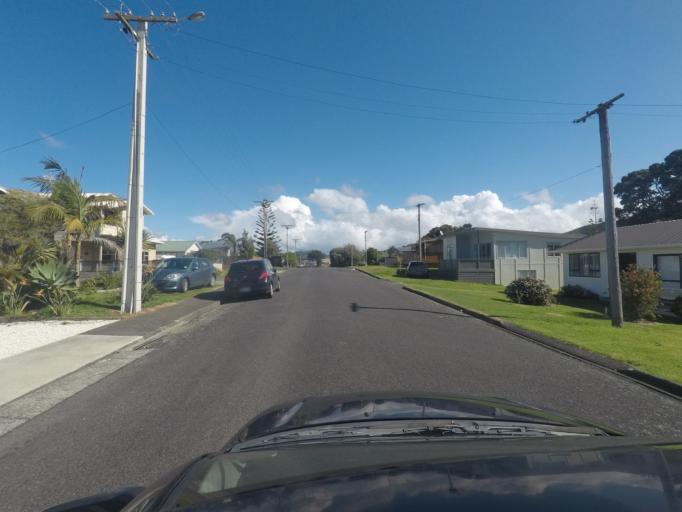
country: NZ
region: Bay of Plenty
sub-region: Western Bay of Plenty District
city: Waihi Beach
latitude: -37.4001
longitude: 175.9386
